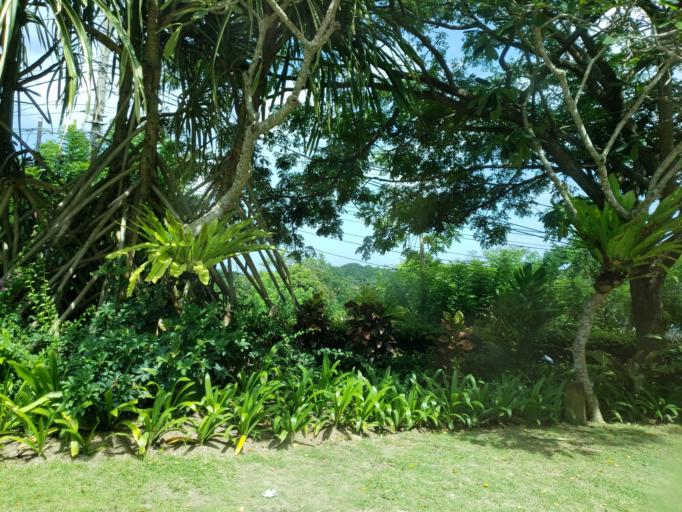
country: ID
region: Bali
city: Pecatu
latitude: -8.8429
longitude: 115.1216
